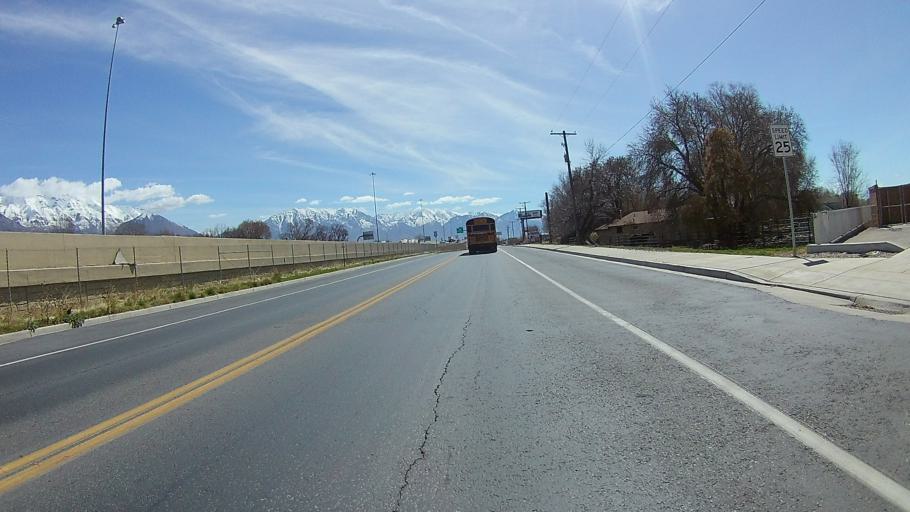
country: US
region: Utah
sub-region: Utah County
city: American Fork
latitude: 40.3695
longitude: -111.8004
